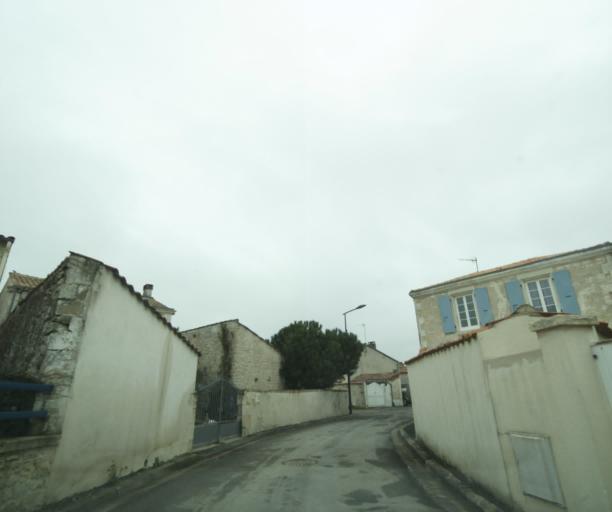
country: FR
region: Poitou-Charentes
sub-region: Departement de la Charente-Maritime
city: Lagord
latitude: 46.1844
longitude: -1.1402
